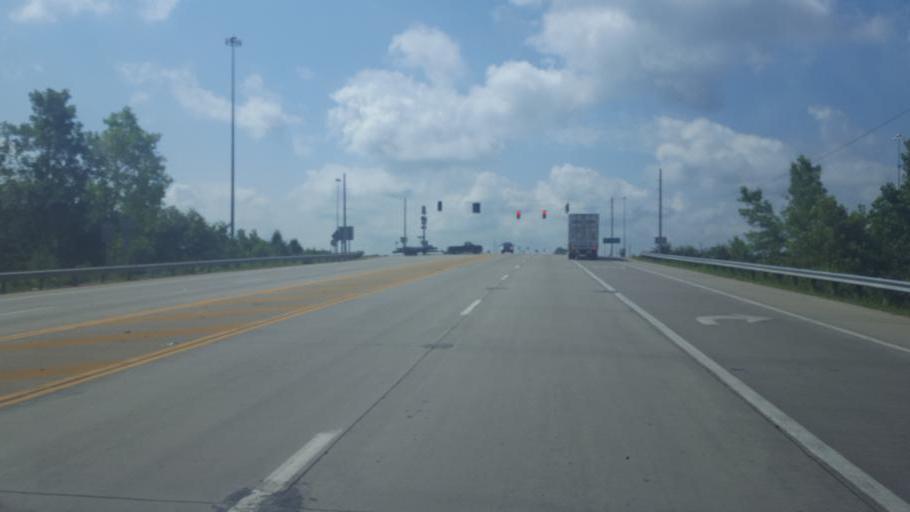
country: US
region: Ohio
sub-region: Fairfield County
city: Millersport
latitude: 39.9443
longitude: -82.5352
